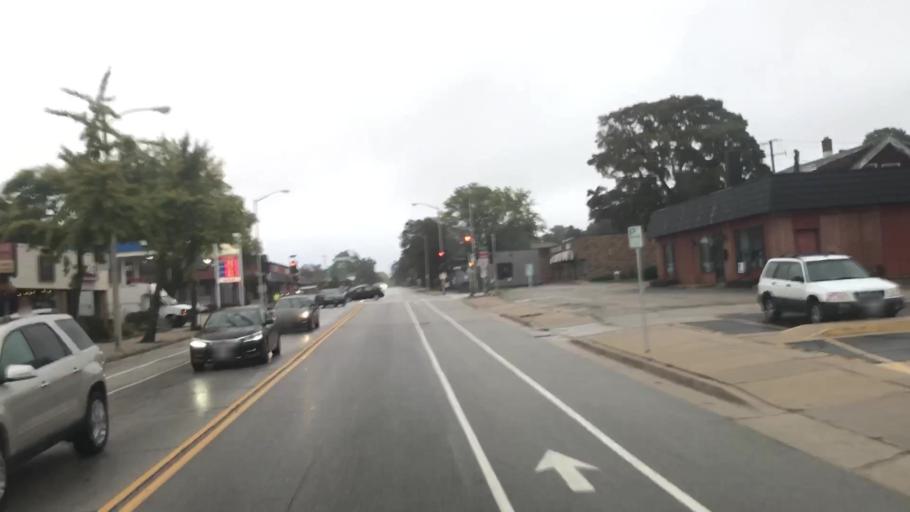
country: US
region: Wisconsin
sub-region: Milwaukee County
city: Wauwatosa
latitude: 43.0605
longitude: -88.0235
